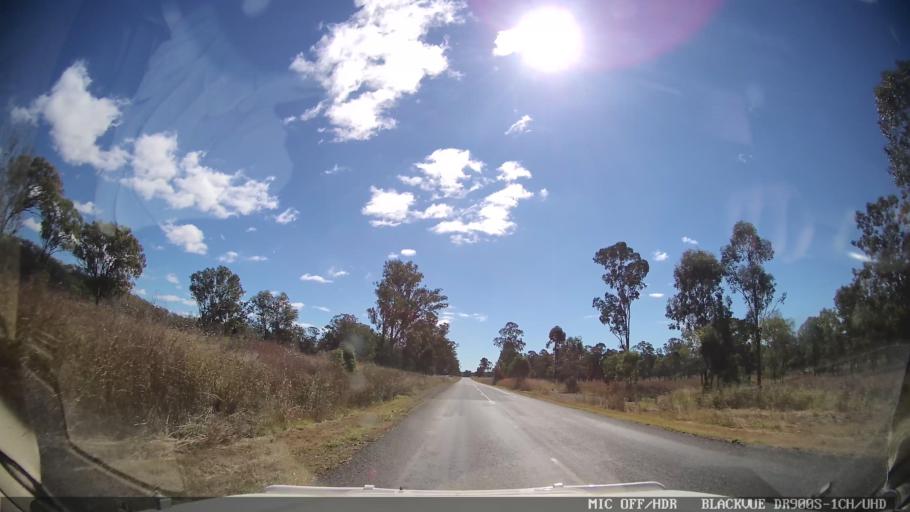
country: AU
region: Queensland
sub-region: Gladstone
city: Toolooa
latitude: -24.4444
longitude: 151.3421
